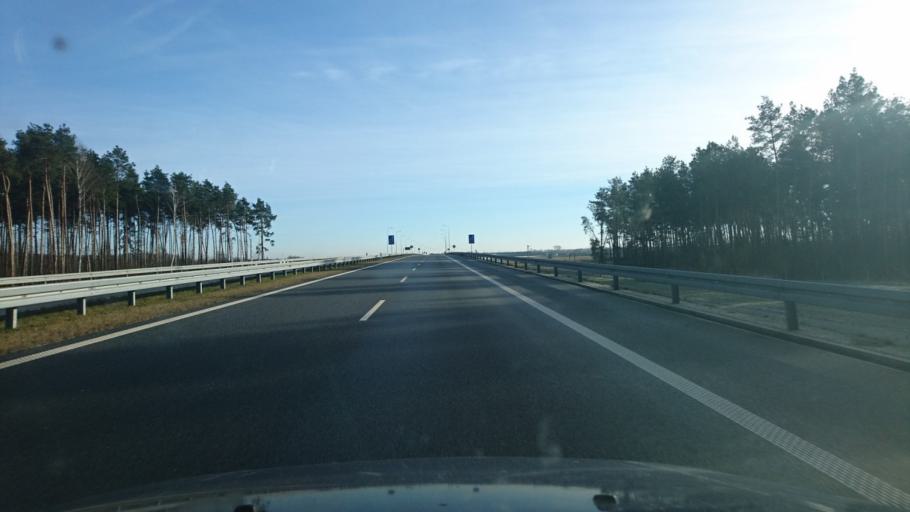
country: PL
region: Greater Poland Voivodeship
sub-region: Powiat kepinski
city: Kepno
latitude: 51.3247
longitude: 17.9939
